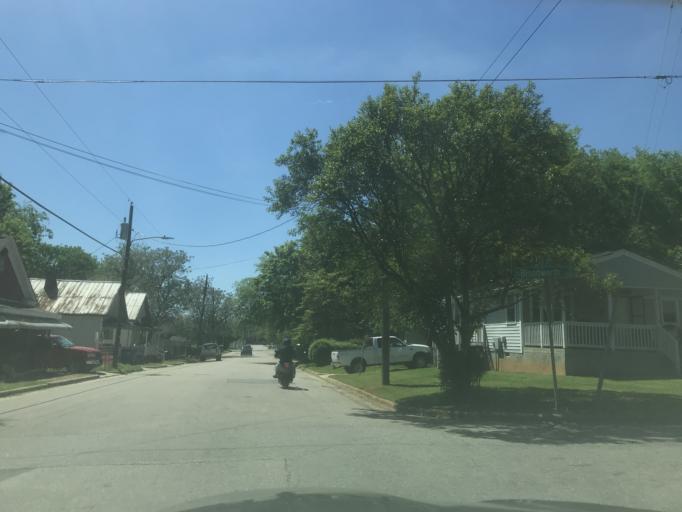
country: US
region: North Carolina
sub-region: Wake County
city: Raleigh
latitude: 35.7658
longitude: -78.6339
